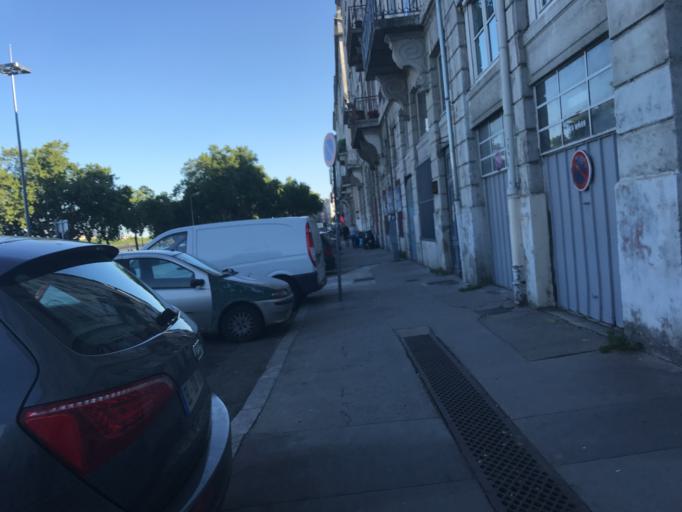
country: FR
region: Rhone-Alpes
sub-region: Departement du Rhone
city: Caluire-et-Cuire
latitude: 45.7721
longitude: 4.8378
